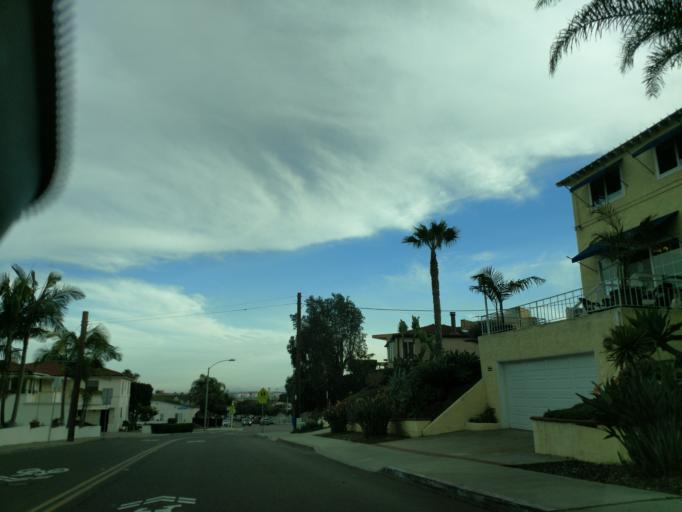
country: US
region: California
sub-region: San Diego County
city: Coronado
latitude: 32.7232
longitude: -117.2345
